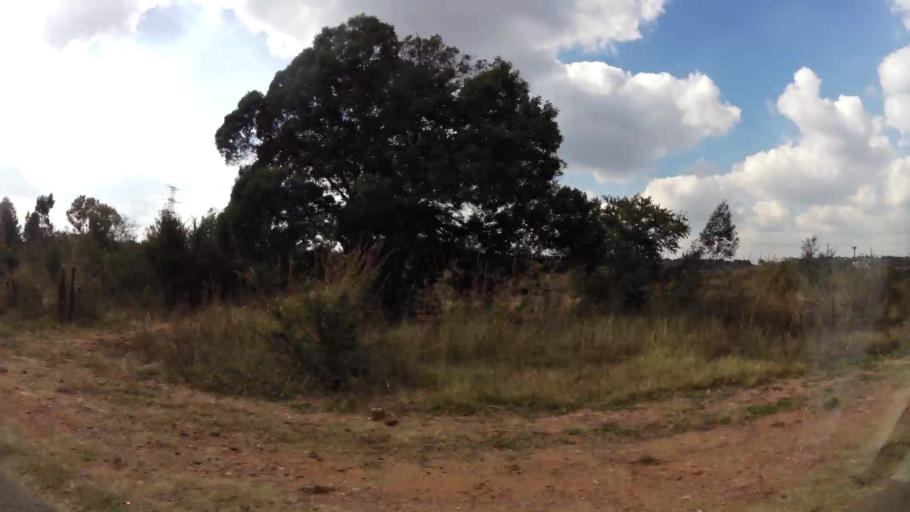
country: ZA
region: Gauteng
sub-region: City of Tshwane Metropolitan Municipality
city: Centurion
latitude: -25.8195
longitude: 28.2403
